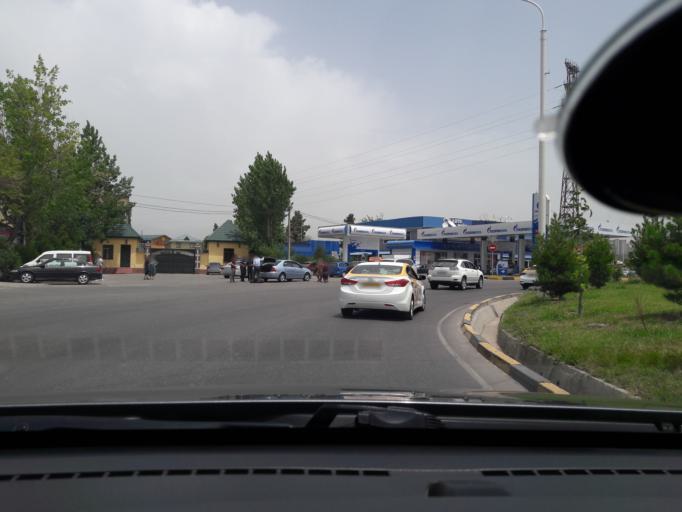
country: TJ
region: Dushanbe
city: Dushanbe
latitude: 38.5603
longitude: 68.7682
